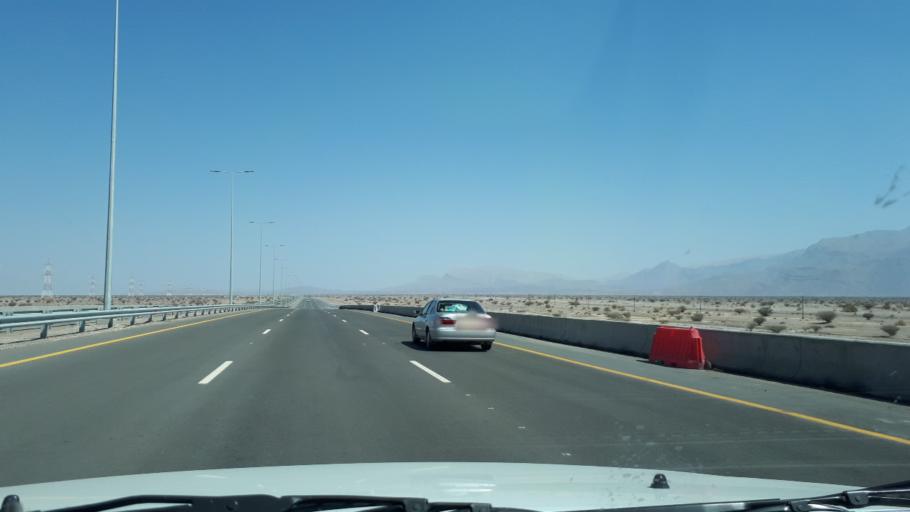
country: OM
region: Ash Sharqiyah
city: Badiyah
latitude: 22.3216
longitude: 59.1350
